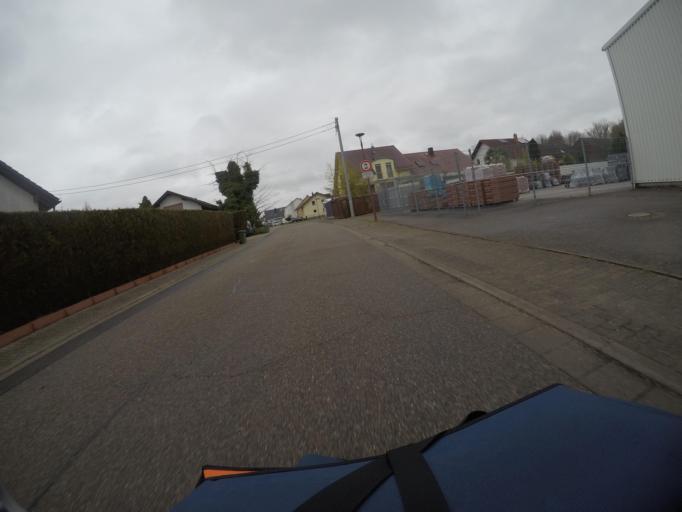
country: DE
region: Rheinland-Pfalz
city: Germersheim
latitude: 49.2310
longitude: 8.4079
